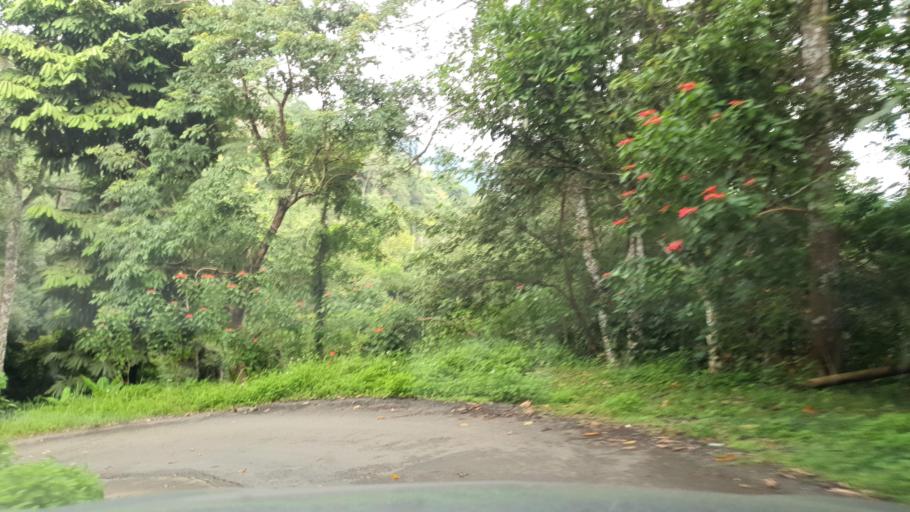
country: TH
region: Chiang Mai
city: Mae On
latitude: 18.9477
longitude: 99.3074
